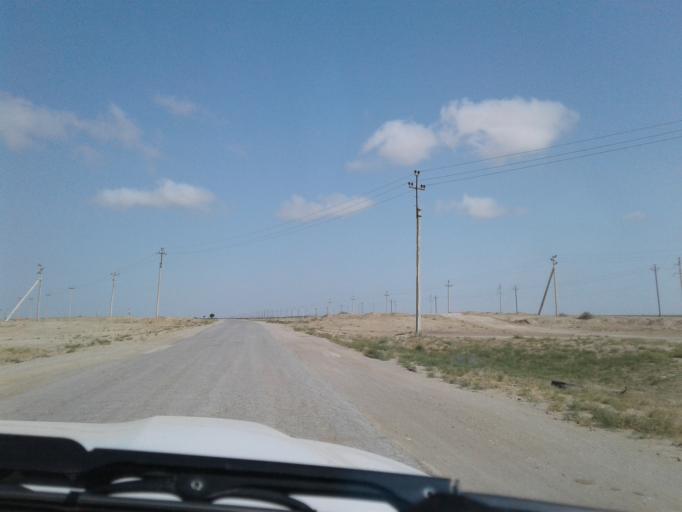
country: IR
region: Golestan
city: Gomishan
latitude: 37.7230
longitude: 53.9395
